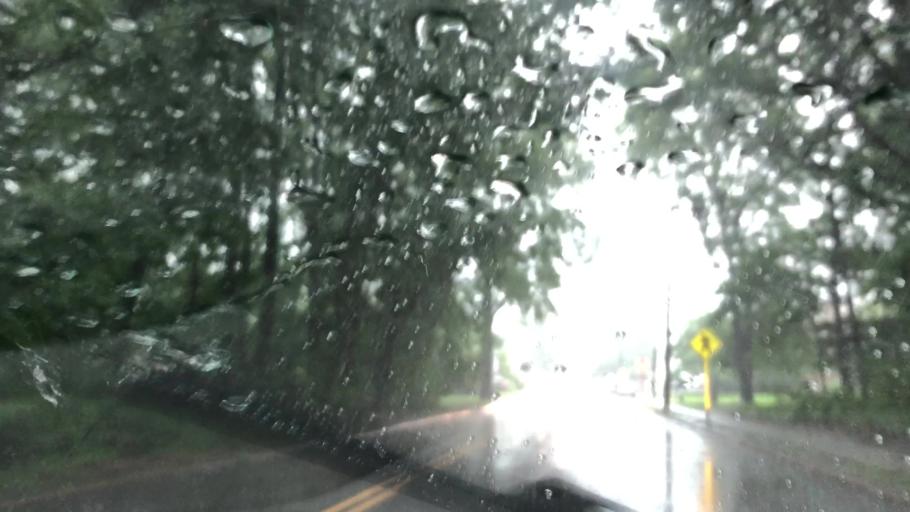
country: US
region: New Jersey
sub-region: Bergen County
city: Elmwood Park
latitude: 40.9131
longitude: -74.1149
